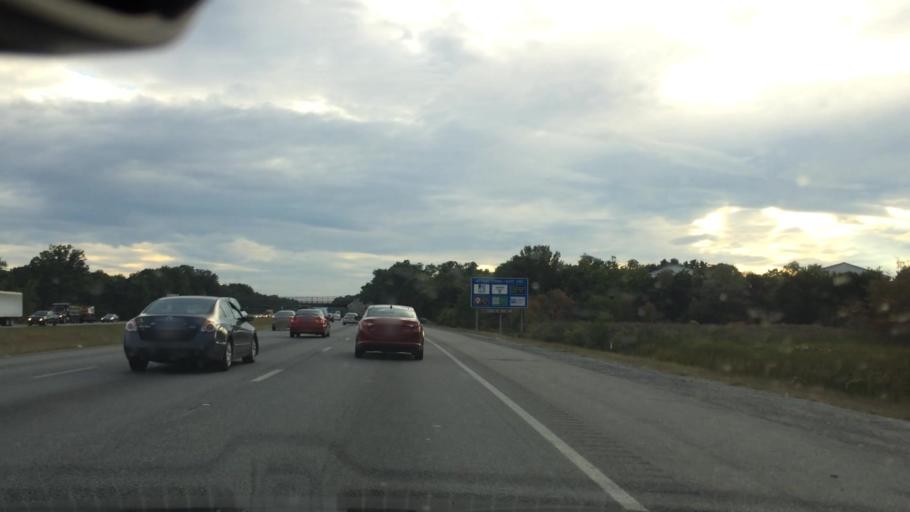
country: US
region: Massachusetts
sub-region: Middlesex County
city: Lowell
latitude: 42.6154
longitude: -71.2988
